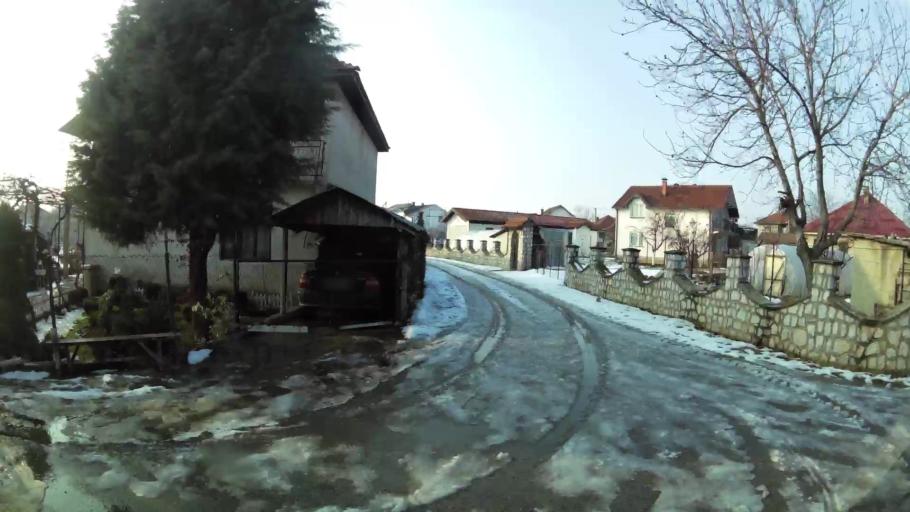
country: MK
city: Miladinovci
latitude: 41.9766
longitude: 21.6480
